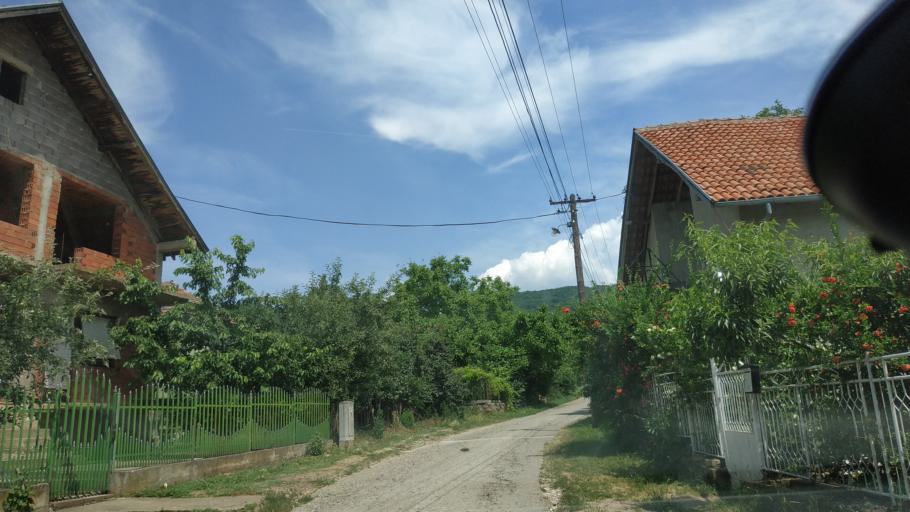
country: RS
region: Central Serbia
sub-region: Nisavski Okrug
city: Aleksinac
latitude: 43.5988
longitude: 21.6944
